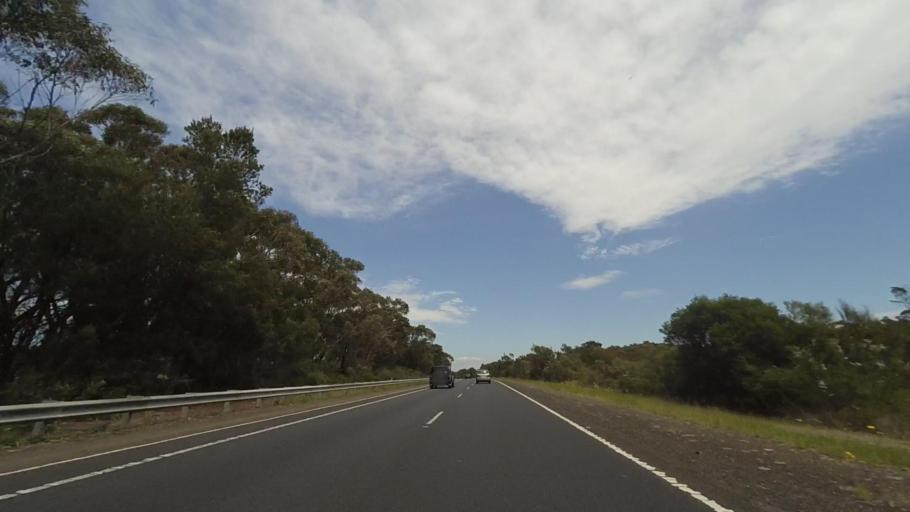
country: AU
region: New South Wales
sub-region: Wollongong
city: Helensburgh
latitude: -34.2458
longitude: 150.9395
